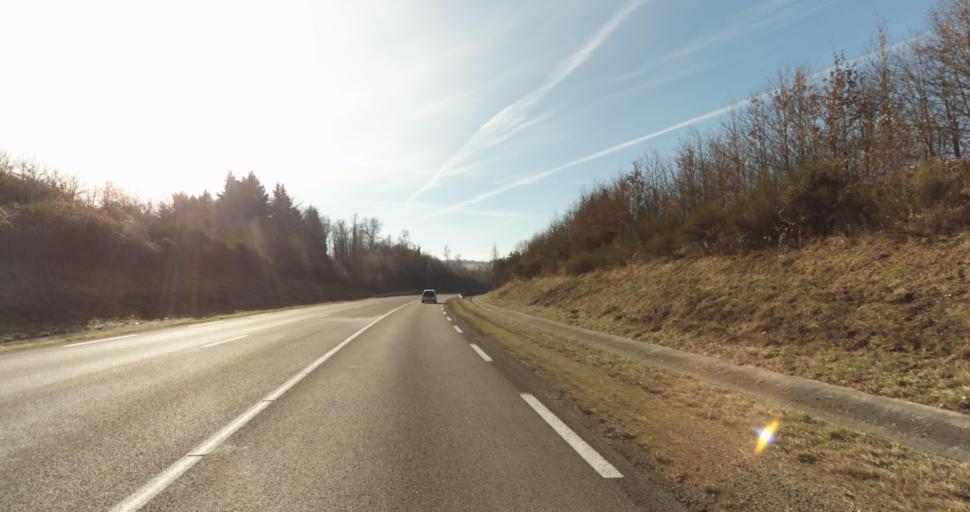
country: FR
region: Limousin
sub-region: Departement de la Haute-Vienne
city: Aixe-sur-Vienne
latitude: 45.8323
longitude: 1.1476
